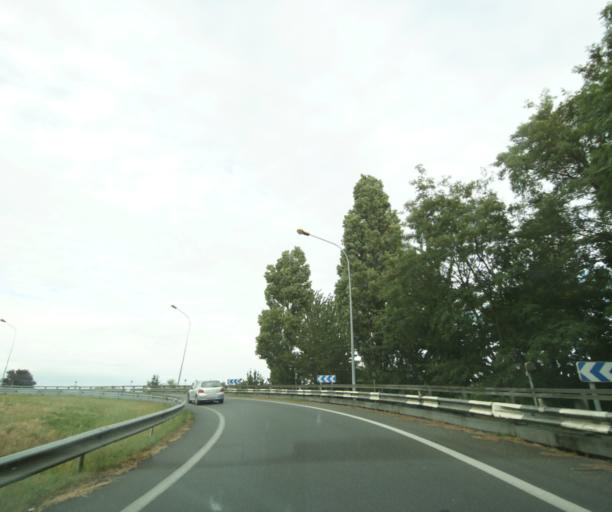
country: FR
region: Poitou-Charentes
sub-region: Departement de la Charente-Maritime
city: Sainte-Soulle
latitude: 46.2003
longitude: -1.0277
